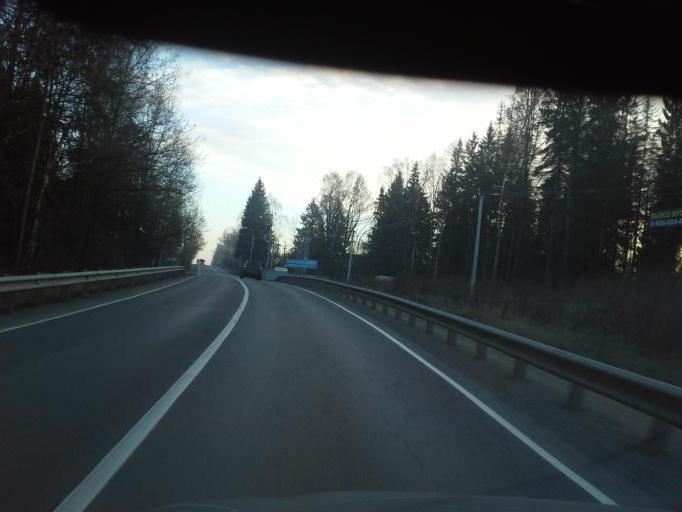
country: RU
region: Moskovskaya
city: Zhavoronki
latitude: 55.6045
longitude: 37.1056
